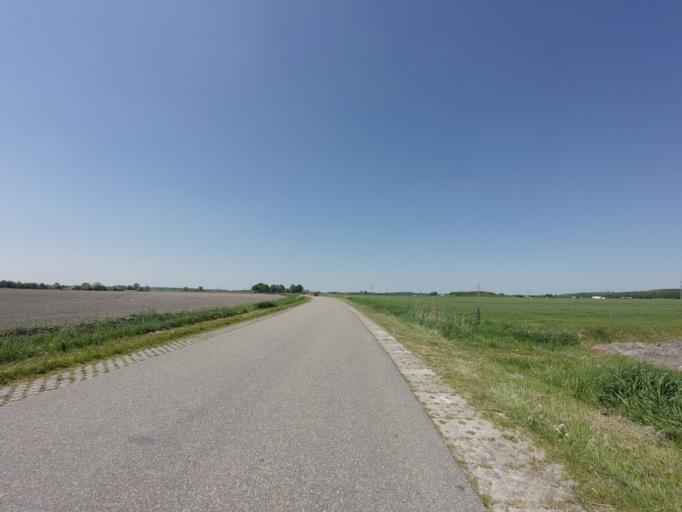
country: NL
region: Zeeland
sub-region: Gemeente Goes
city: Goes
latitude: 51.4794
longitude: 3.8646
